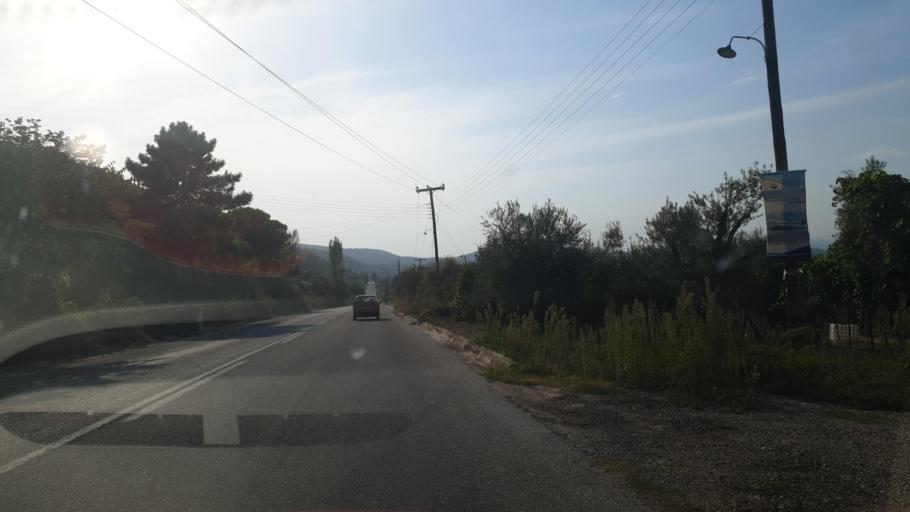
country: GR
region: Central Macedonia
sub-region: Nomos Chalkidikis
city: Neos Marmaras
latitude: 40.1818
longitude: 23.8030
